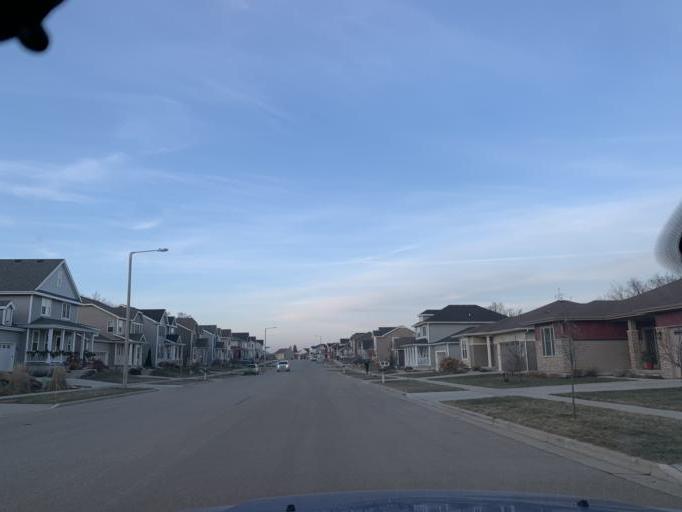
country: US
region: Wisconsin
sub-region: Dane County
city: Verona
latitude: 43.0546
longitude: -89.5626
